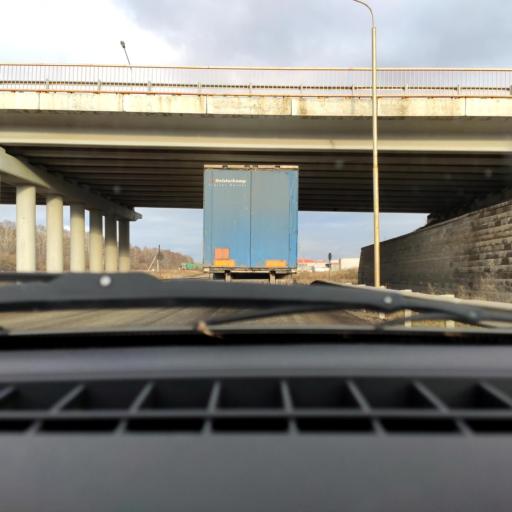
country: RU
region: Bashkortostan
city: Iglino
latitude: 54.7721
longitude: 56.2577
